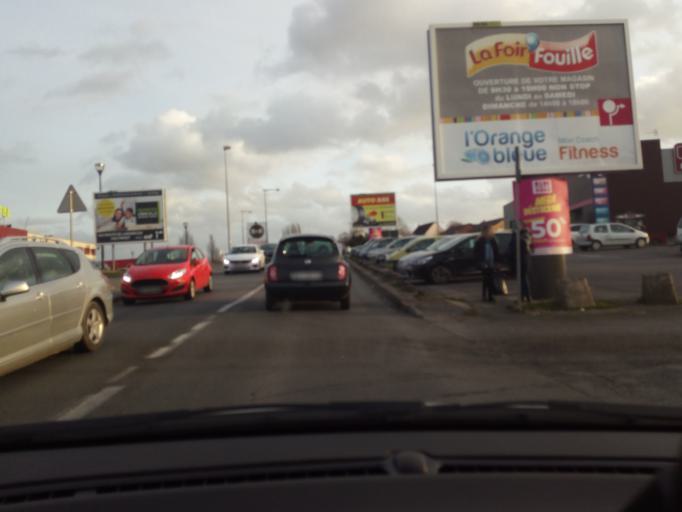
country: FR
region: Nord-Pas-de-Calais
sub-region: Departement du Nord
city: Hautmont
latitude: 50.2519
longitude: 3.9411
